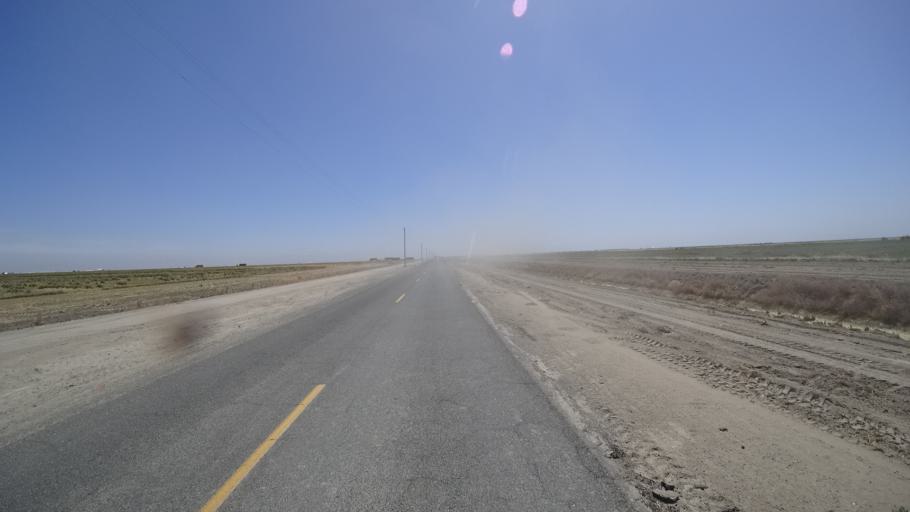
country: US
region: California
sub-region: Kings County
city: Stratford
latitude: 36.1379
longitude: -119.6965
